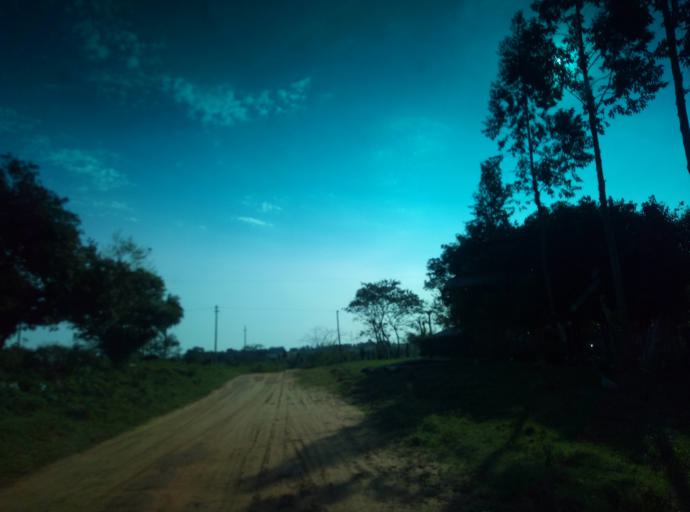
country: PY
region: Caaguazu
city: Doctor Cecilio Baez
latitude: -25.1647
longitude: -56.2314
